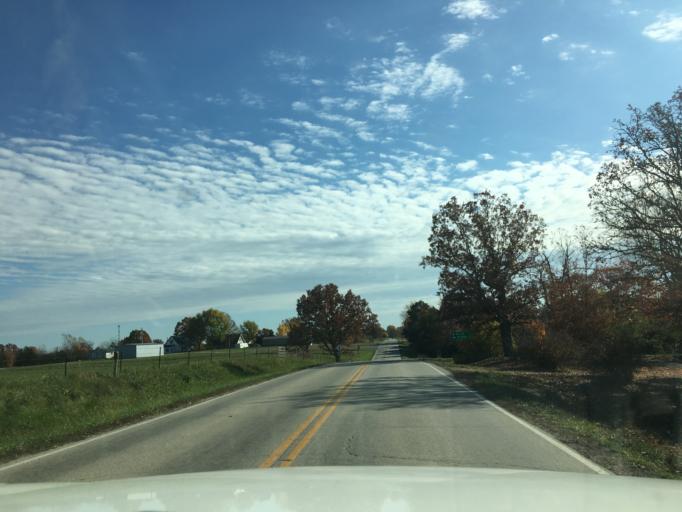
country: US
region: Missouri
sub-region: Maries County
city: Belle
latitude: 38.3027
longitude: -91.7265
